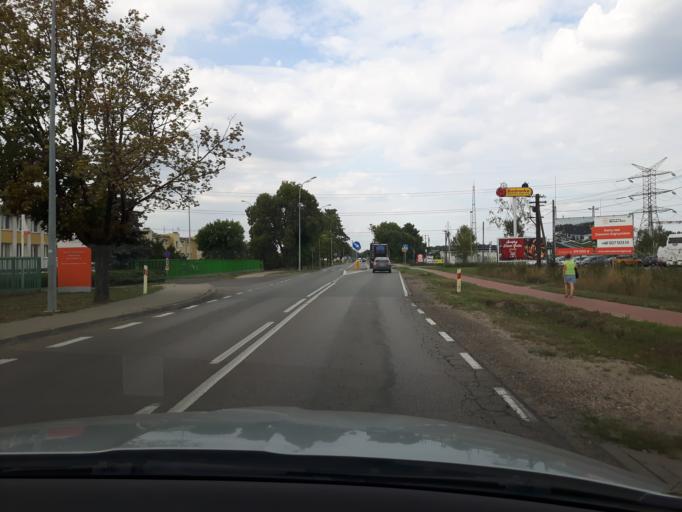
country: PL
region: Masovian Voivodeship
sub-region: Powiat legionowski
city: Stanislawow Pierwszy
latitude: 52.3694
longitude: 21.0288
